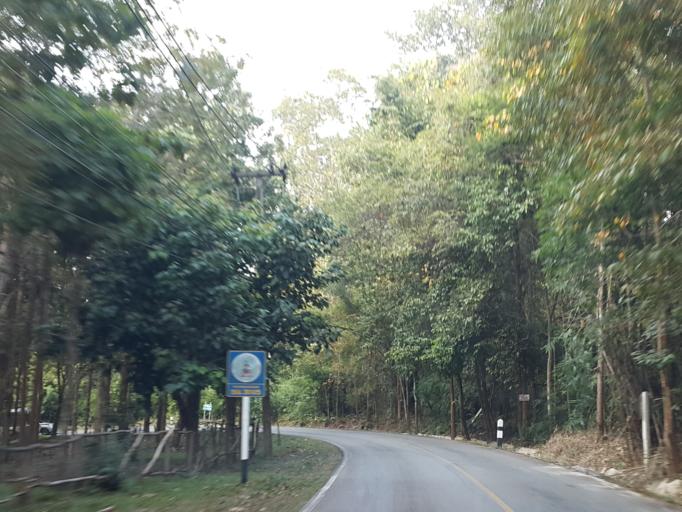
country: TH
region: Chiang Mai
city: Mae On
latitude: 18.8961
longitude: 99.2615
